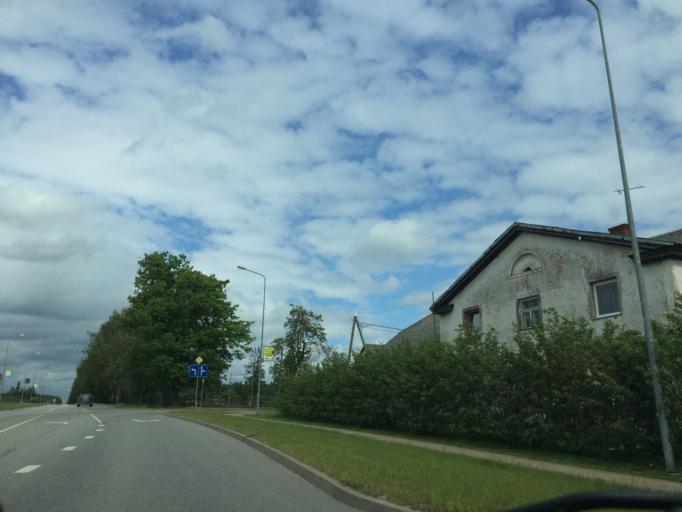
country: LV
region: Valmieras Rajons
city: Valmiera
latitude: 57.5502
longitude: 25.4404
